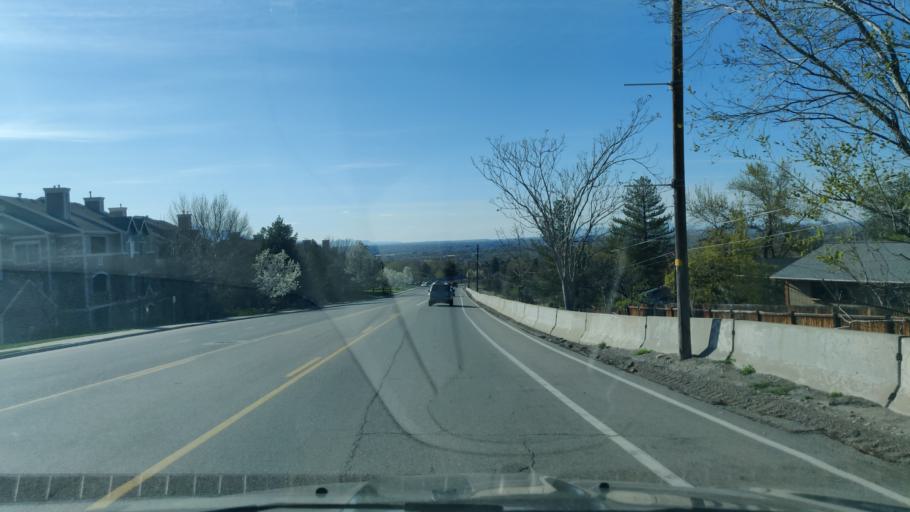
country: US
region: Utah
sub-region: Salt Lake County
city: Little Cottonwood Creek Valley
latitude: 40.6138
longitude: -111.8299
